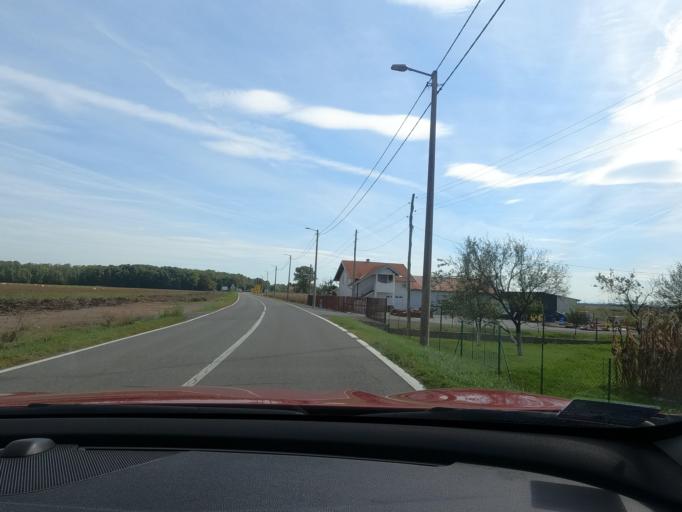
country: HR
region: Sisacko-Moslavacka
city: Budasevo
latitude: 45.4869
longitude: 16.4620
